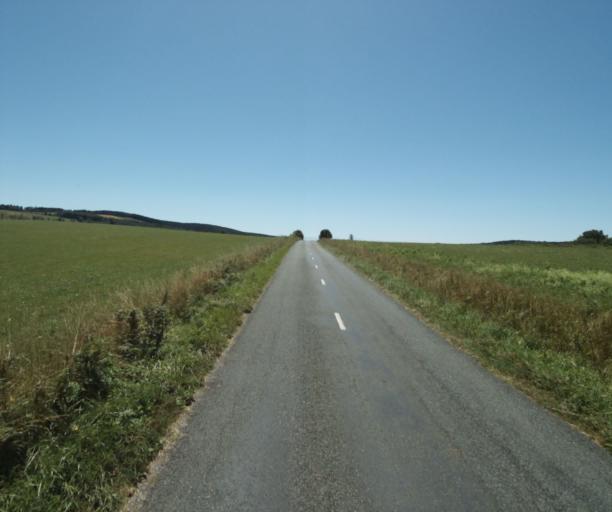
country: FR
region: Midi-Pyrenees
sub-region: Departement du Tarn
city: Dourgne
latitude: 43.4390
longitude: 2.1770
